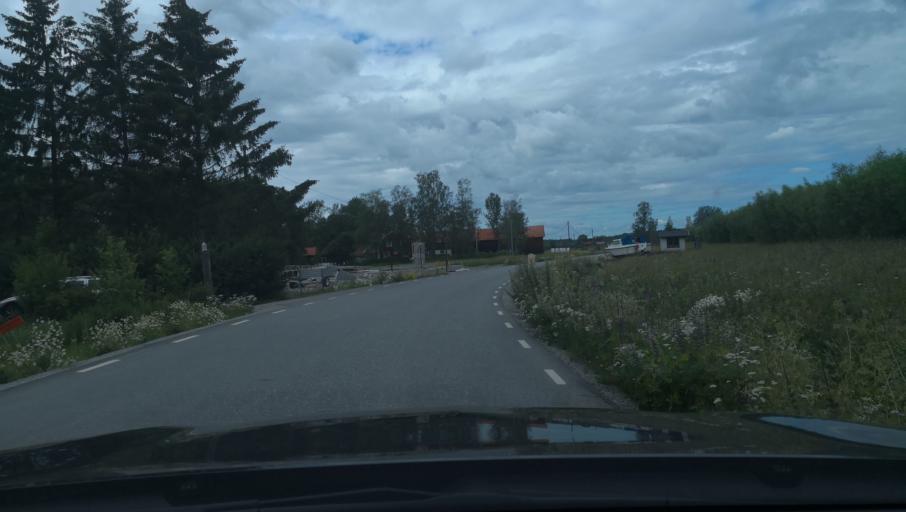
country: SE
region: Vaestmanland
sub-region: Hallstahammars Kommun
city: Hallstahammar
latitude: 59.5994
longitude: 16.1502
